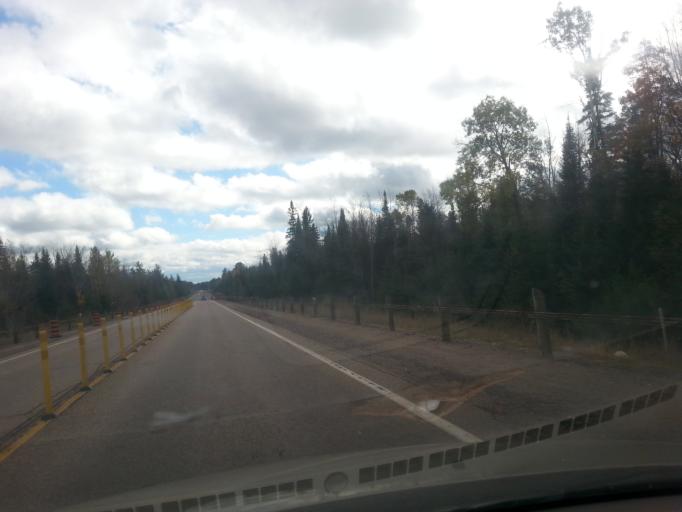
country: CA
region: Ontario
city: Pembroke
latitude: 45.8016
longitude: -77.1975
